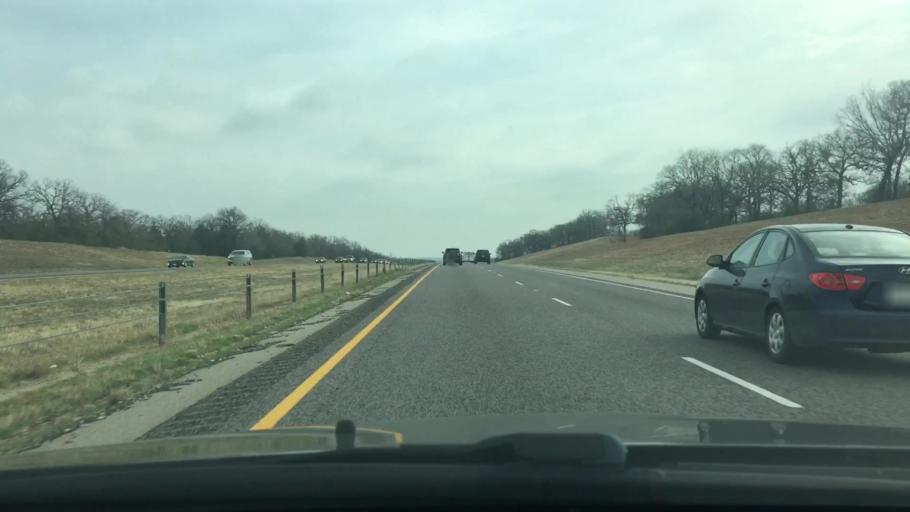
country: US
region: Texas
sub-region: Leon County
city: Buffalo
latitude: 31.5321
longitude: -96.1175
